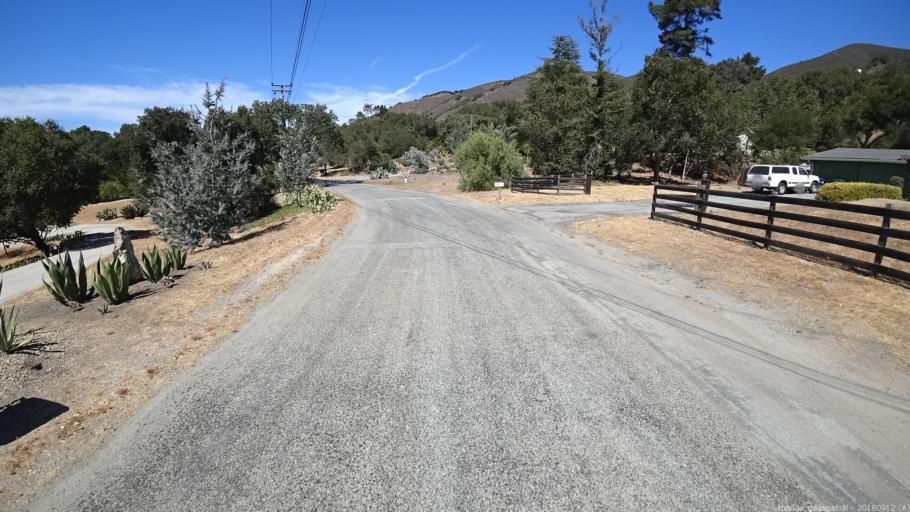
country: US
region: California
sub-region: Monterey County
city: Carmel Valley Village
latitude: 36.4992
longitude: -121.7451
